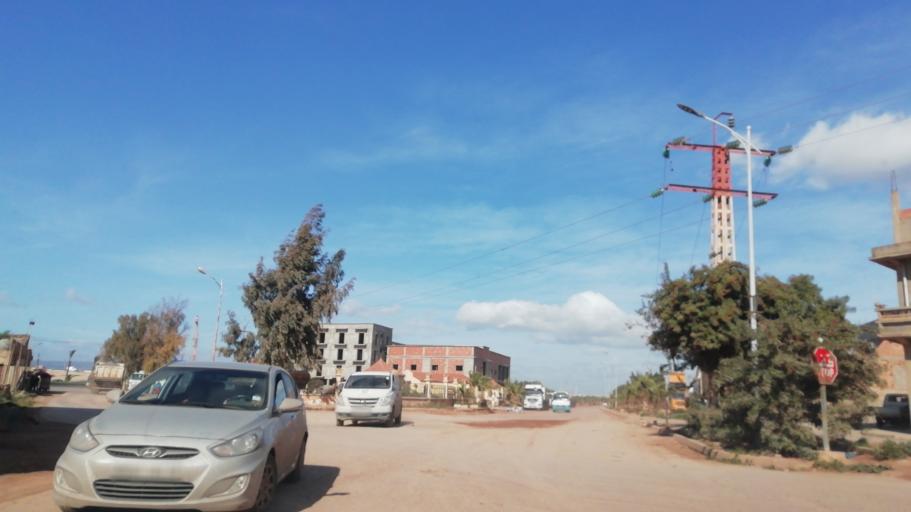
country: DZ
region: Oran
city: Es Senia
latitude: 35.6223
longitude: -0.5840
